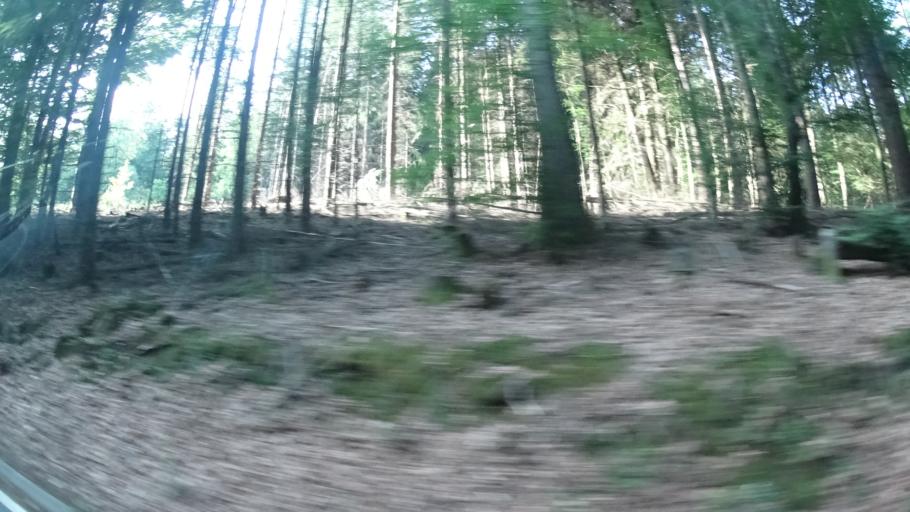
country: DE
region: Hesse
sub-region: Regierungsbezirk Darmstadt
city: Wald-Michelbach
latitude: 49.5567
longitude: 8.8928
